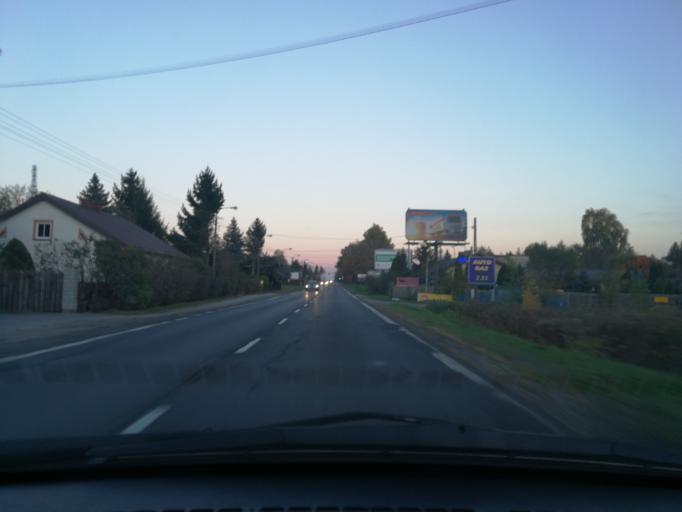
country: PL
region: Lodz Voivodeship
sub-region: Powiat lodzki wschodni
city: Andrespol
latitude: 51.7951
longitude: 19.5706
